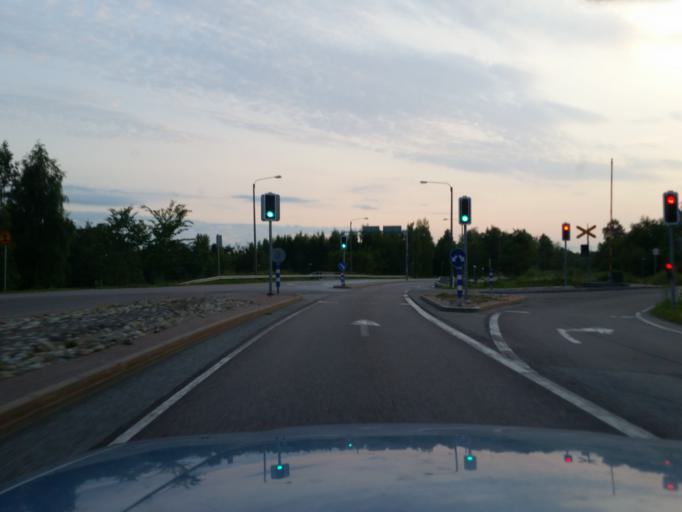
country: FI
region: Southern Savonia
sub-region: Savonlinna
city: Savonlinna
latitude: 61.8777
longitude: 28.8209
